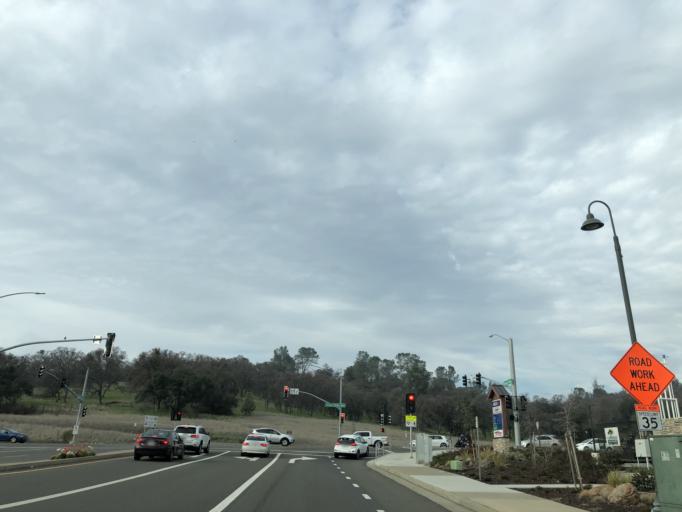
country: US
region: California
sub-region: El Dorado County
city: El Dorado Hills
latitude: 38.7008
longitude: -121.1065
